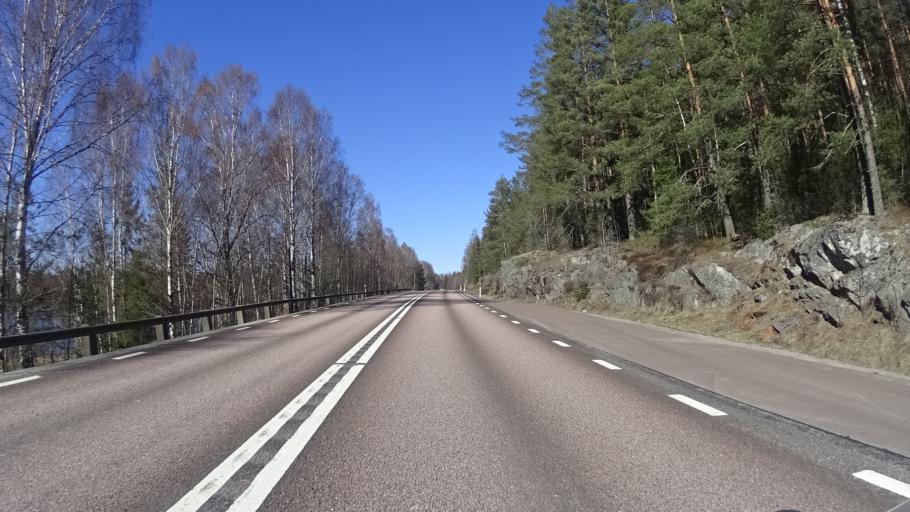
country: SE
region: Vaermland
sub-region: Sunne Kommun
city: Sunne
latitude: 59.6451
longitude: 12.9444
